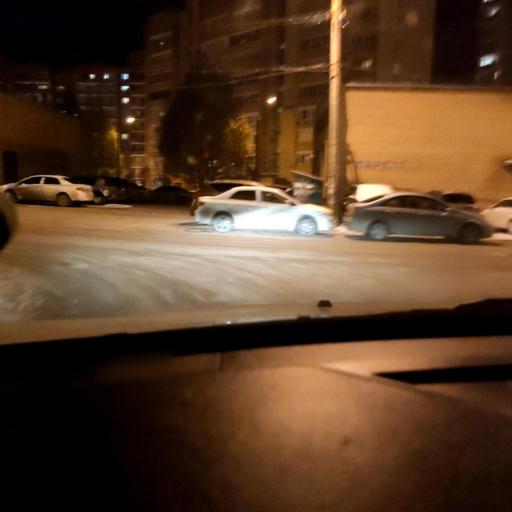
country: RU
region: Samara
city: Samara
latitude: 53.2448
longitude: 50.1867
